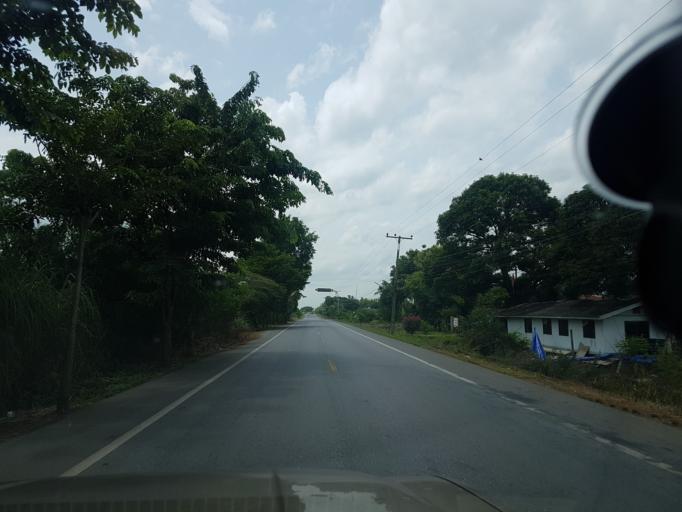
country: TH
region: Sara Buri
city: Nong Khae
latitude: 14.2491
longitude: 100.8918
